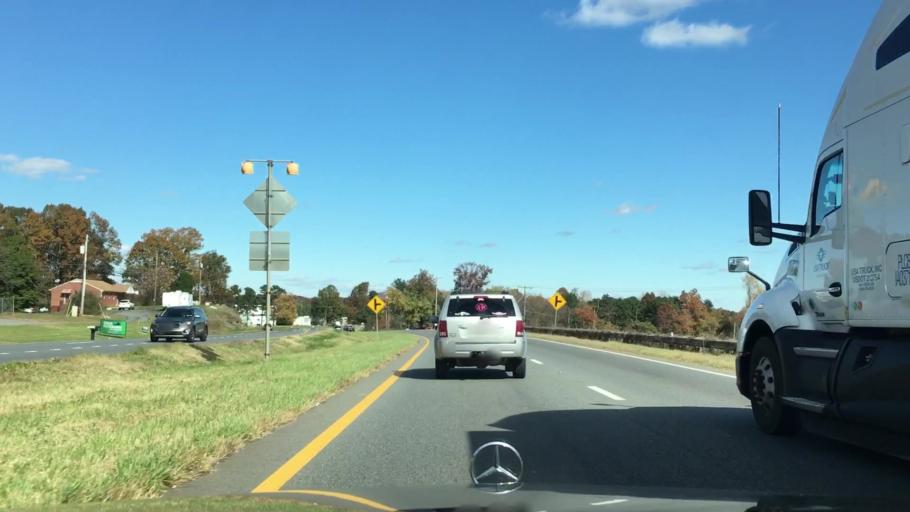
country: US
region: Virginia
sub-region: Campbell County
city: Rustburg
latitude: 37.2816
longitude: -79.1673
